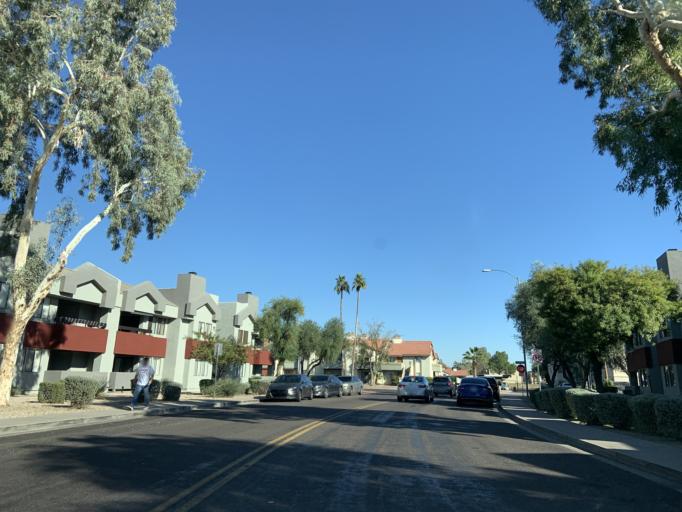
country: US
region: Arizona
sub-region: Maricopa County
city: Tempe
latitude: 33.3985
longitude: -111.8666
